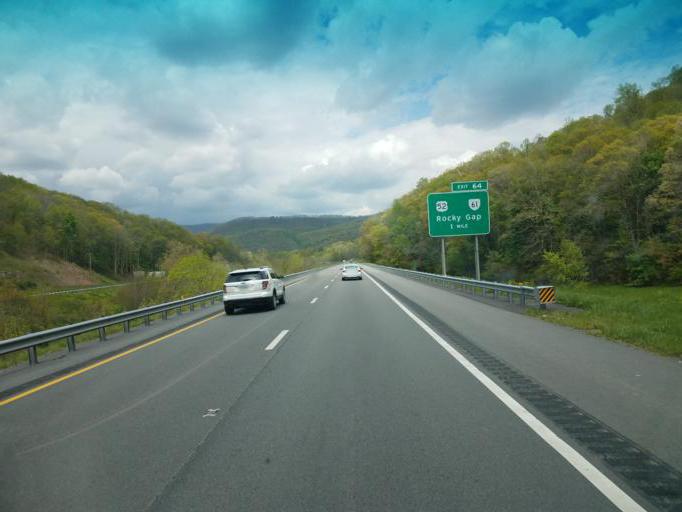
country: US
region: Virginia
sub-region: Bland County
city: Bland
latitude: 37.2272
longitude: -81.0941
